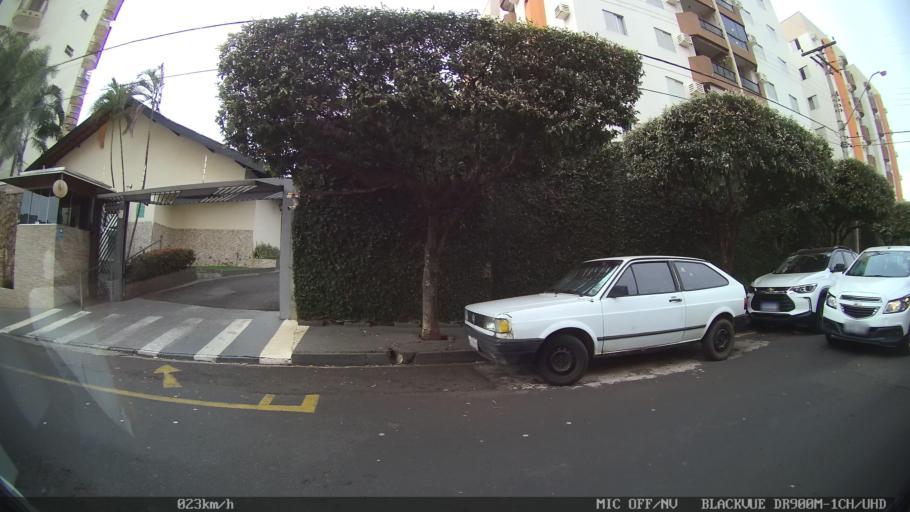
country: BR
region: Sao Paulo
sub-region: Sao Jose Do Rio Preto
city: Sao Jose do Rio Preto
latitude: -20.8309
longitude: -49.3890
